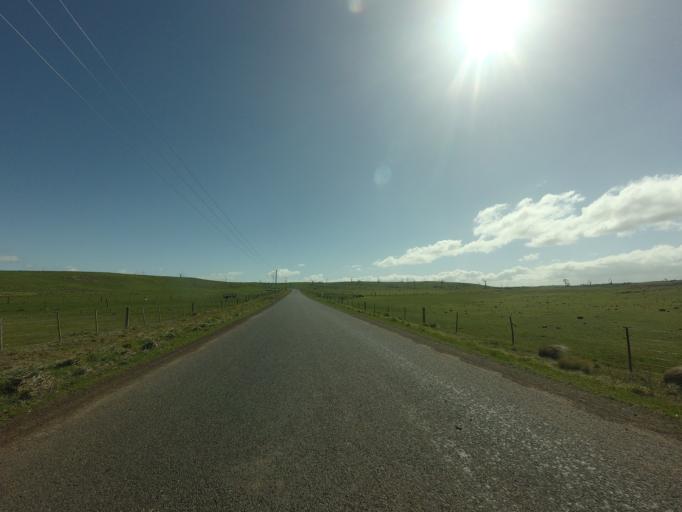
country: AU
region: Tasmania
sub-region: Northern Midlands
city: Evandale
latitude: -41.8982
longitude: 147.4361
